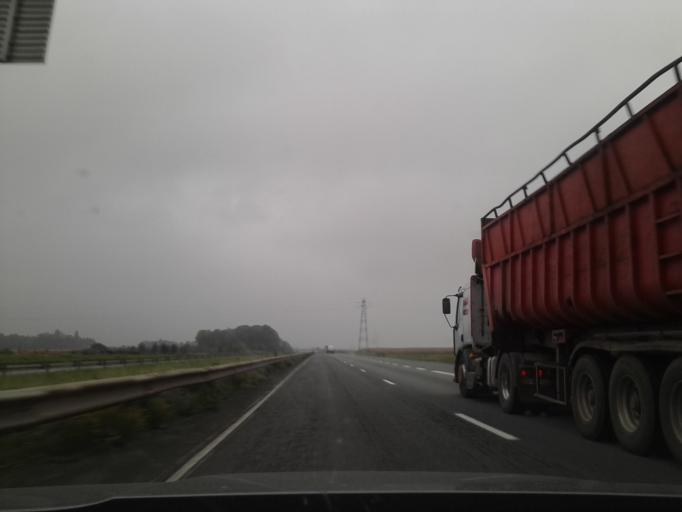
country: FR
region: Nord-Pas-de-Calais
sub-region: Departement du Nord
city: Onnaing
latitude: 50.3663
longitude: 3.5957
